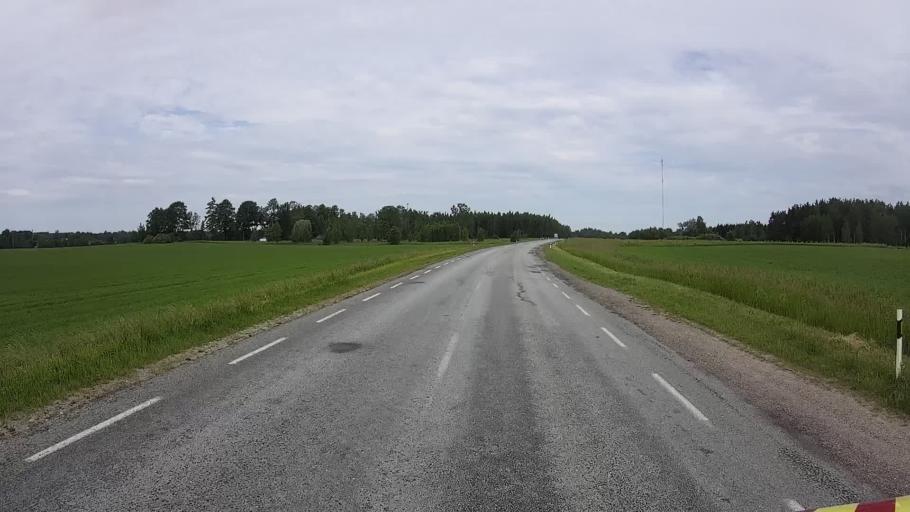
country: EE
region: Viljandimaa
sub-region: Karksi vald
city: Karksi-Nuia
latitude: 58.2304
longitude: 25.6027
